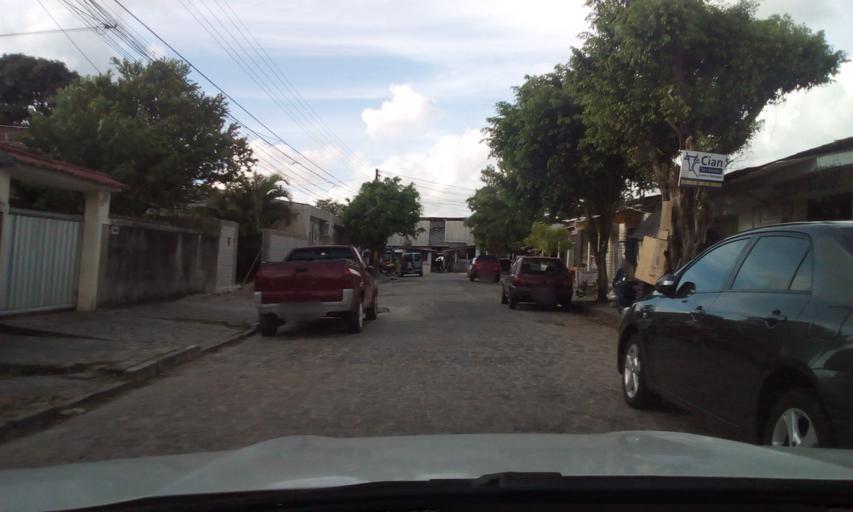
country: BR
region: Paraiba
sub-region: Joao Pessoa
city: Joao Pessoa
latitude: -7.1083
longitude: -34.8570
